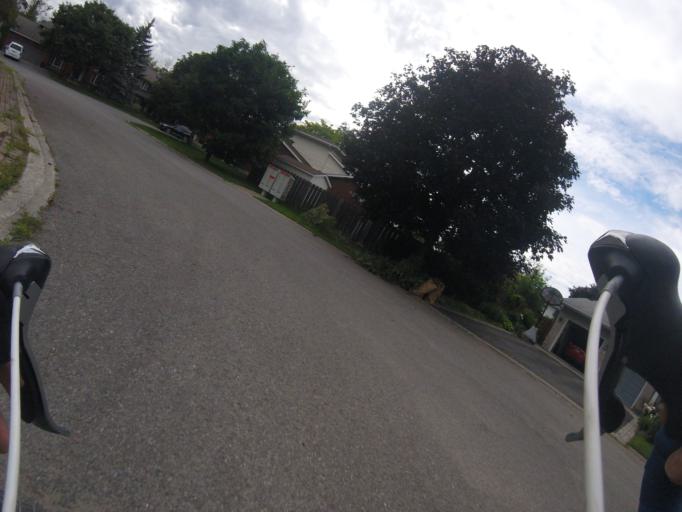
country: CA
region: Ontario
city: Bells Corners
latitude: 45.3316
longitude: -75.7956
